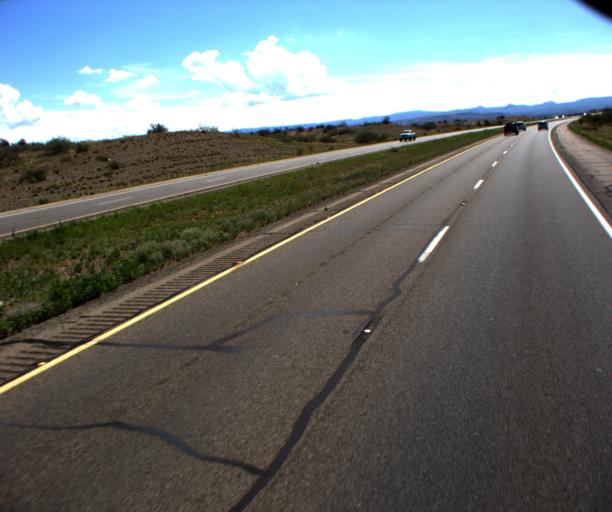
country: US
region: Arizona
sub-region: Yavapai County
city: Spring Valley
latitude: 34.3477
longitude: -112.1483
